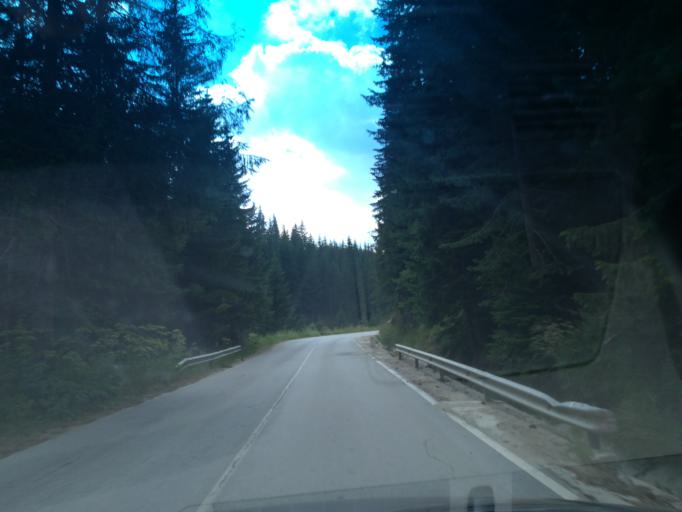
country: BG
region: Smolyan
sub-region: Obshtina Chepelare
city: Chepelare
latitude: 41.6609
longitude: 24.6761
